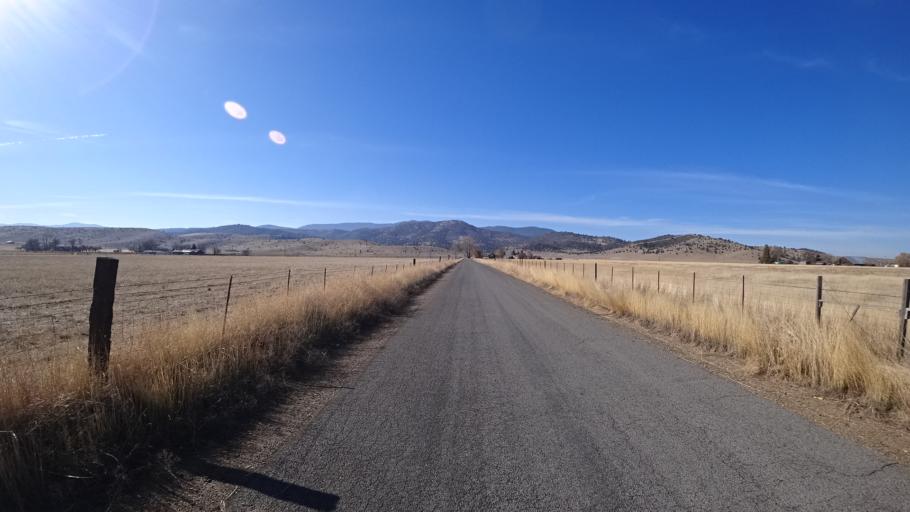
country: US
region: California
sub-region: Siskiyou County
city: Montague
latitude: 41.6181
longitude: -122.5256
